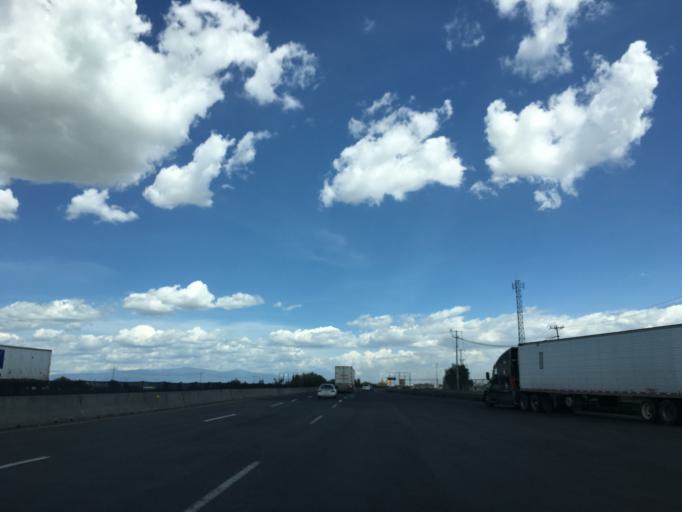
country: MX
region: Mexico
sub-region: Tonanitla
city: Colonia la Asuncion
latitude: 19.6924
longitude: -99.0797
